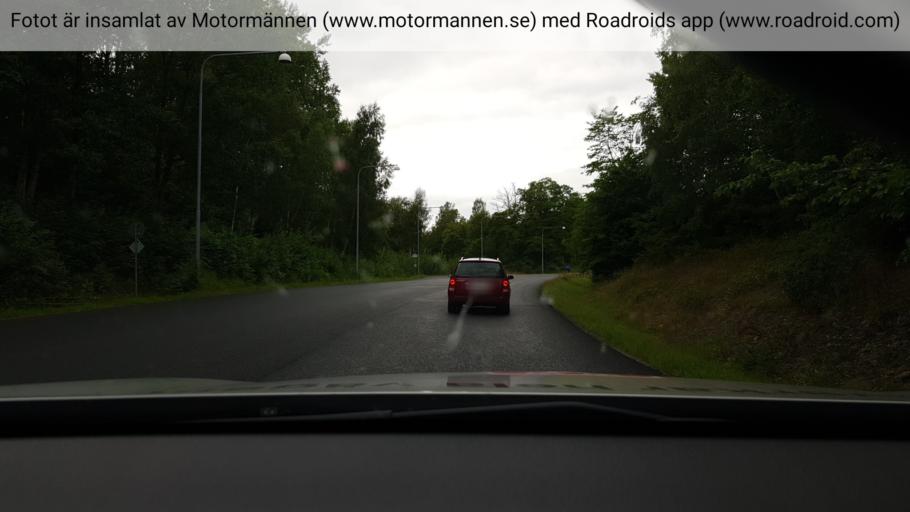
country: SE
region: Stockholm
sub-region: Nynashamns Kommun
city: Nynashamn
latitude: 58.9197
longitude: 17.9261
